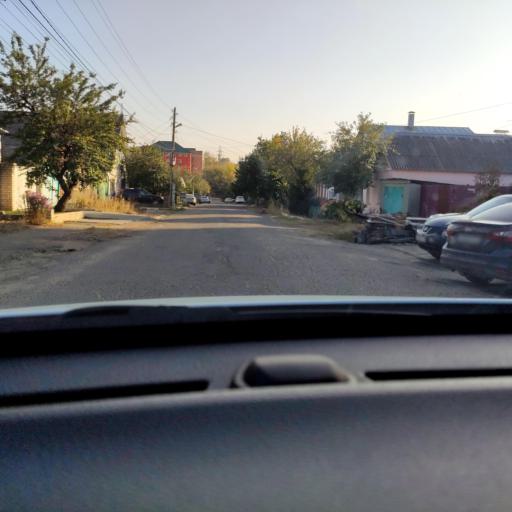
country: RU
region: Voronezj
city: Voronezh
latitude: 51.6914
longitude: 39.1505
